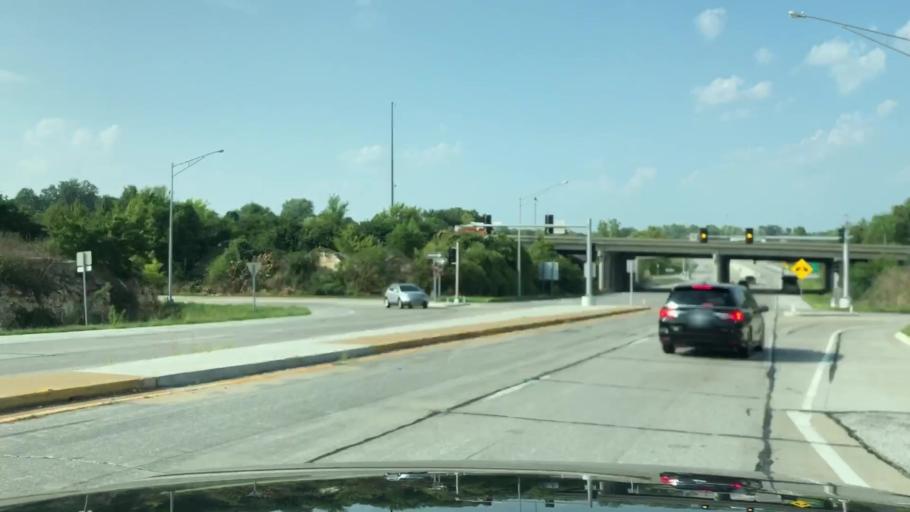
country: US
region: Missouri
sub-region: Saint Charles County
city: Lake Saint Louis
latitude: 38.8041
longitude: -90.8080
